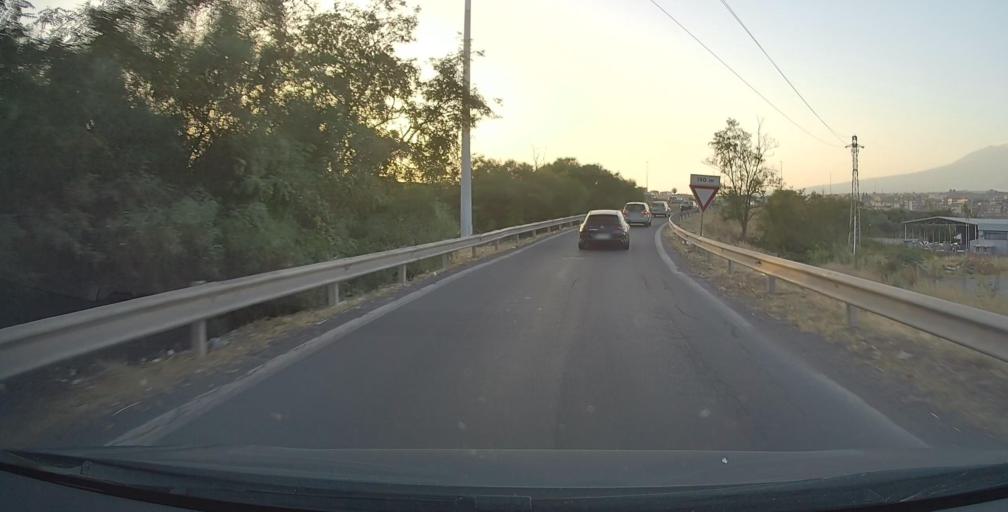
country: IT
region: Sicily
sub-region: Catania
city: Misterbianco
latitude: 37.5088
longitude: 15.0198
